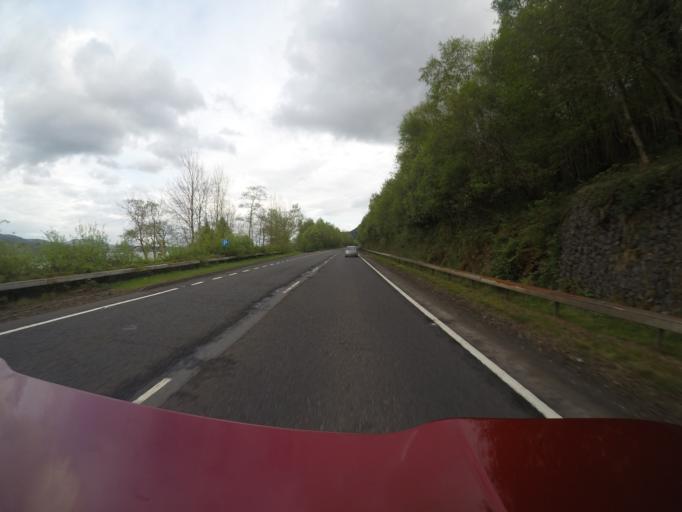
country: GB
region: Scotland
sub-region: Argyll and Bute
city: Helensburgh
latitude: 56.1311
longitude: -4.6557
